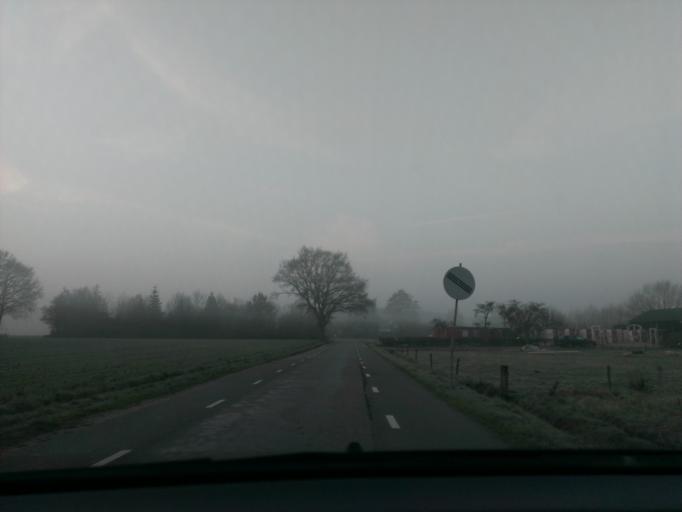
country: NL
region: Gelderland
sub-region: Gemeente Voorst
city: Twello
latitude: 52.2532
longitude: 6.0844
